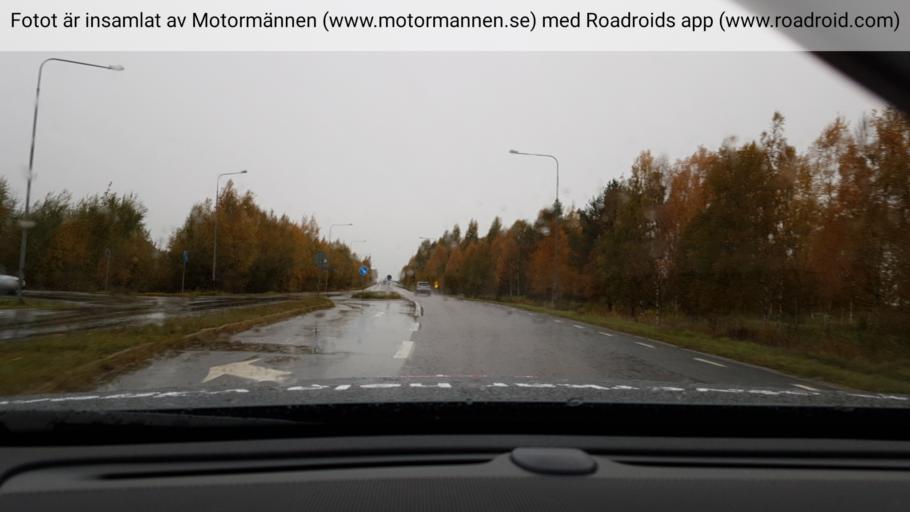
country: SE
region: Norrbotten
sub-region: Lulea Kommun
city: Sodra Sunderbyn
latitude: 65.6580
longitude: 21.9586
